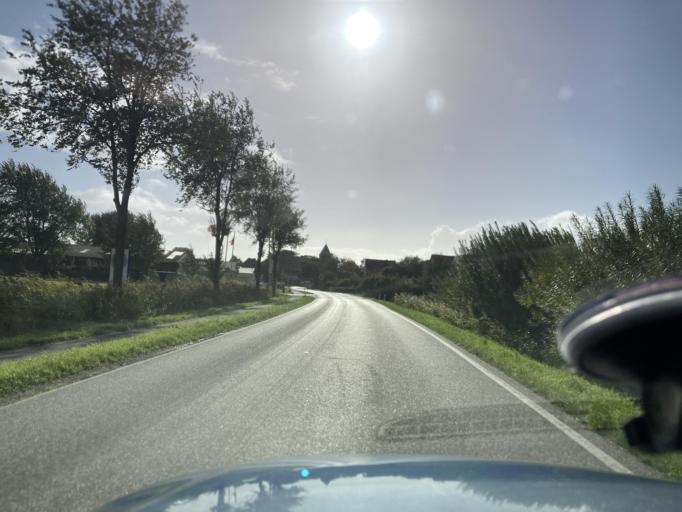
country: DE
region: Schleswig-Holstein
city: Wohrden
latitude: 54.1684
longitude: 9.0017
